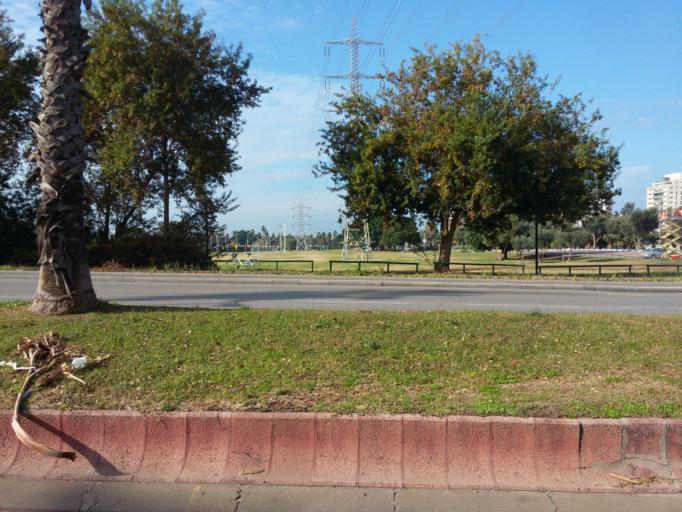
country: IL
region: Tel Aviv
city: Tel Aviv
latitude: 32.1016
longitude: 34.7931
